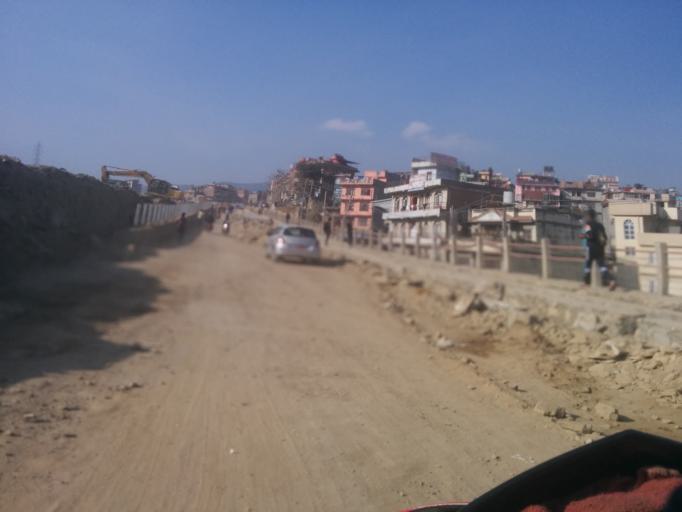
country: NP
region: Central Region
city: Kirtipur
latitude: 27.6906
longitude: 85.2834
